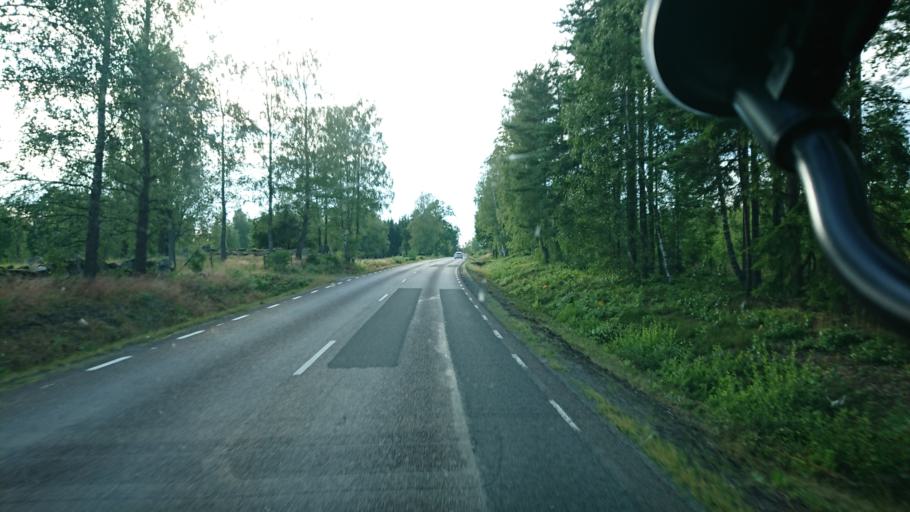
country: SE
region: Kronoberg
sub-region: Vaxjo Kommun
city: Braas
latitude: 57.0184
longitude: 15.0459
